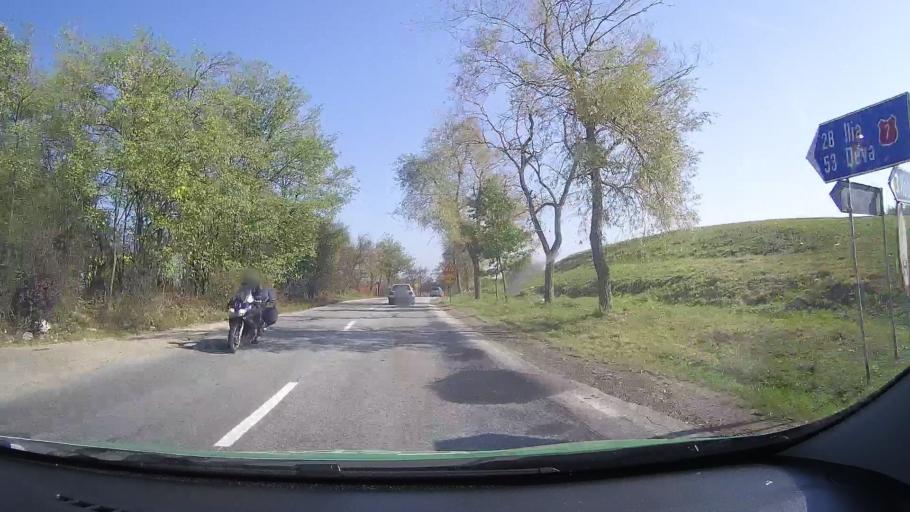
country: RO
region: Timis
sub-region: Comuna Pietroasa
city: Pietroasa
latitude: 45.8822
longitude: 22.3998
